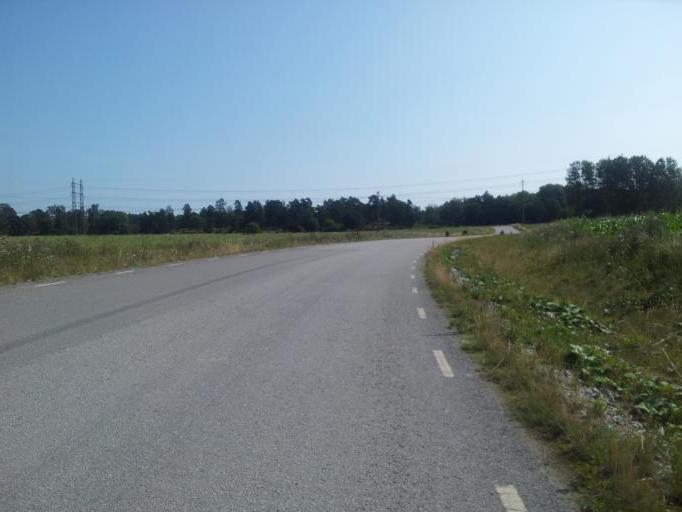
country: SE
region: Uppsala
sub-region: Uppsala Kommun
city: Gamla Uppsala
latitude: 59.9070
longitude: 17.6519
